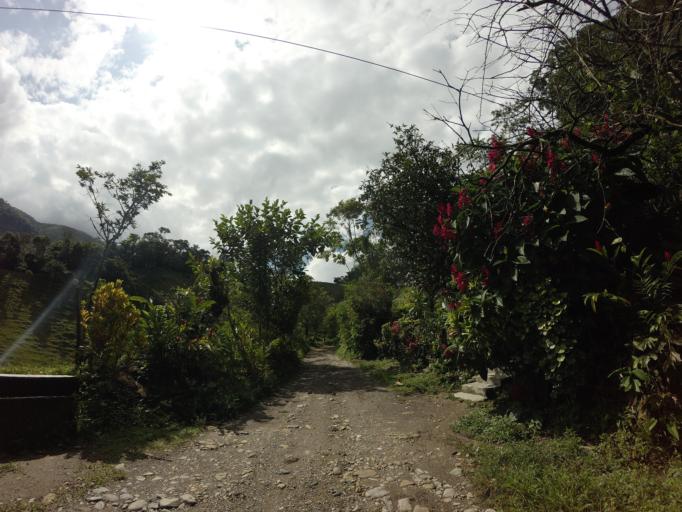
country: CO
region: Antioquia
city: Narino
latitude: 5.5405
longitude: -75.1334
